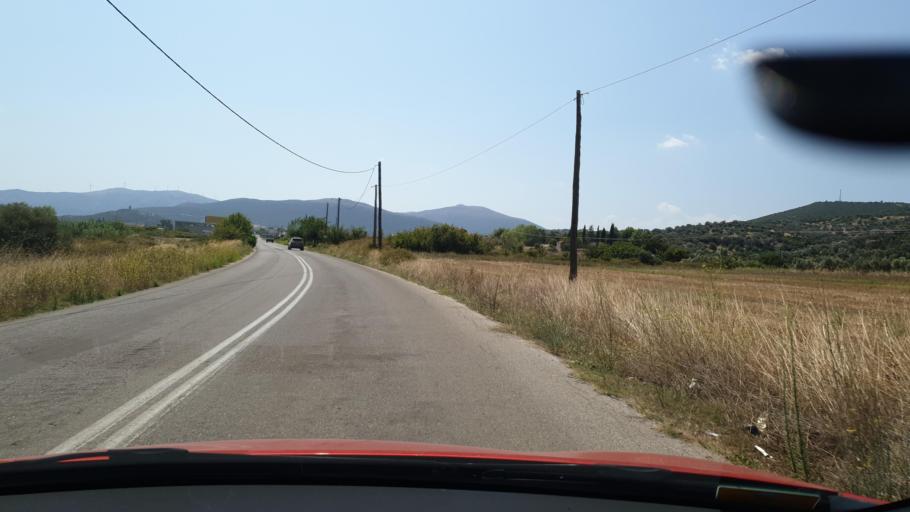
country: GR
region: Central Greece
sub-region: Nomos Evvoias
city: Aliveri
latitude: 38.4157
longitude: 24.1104
